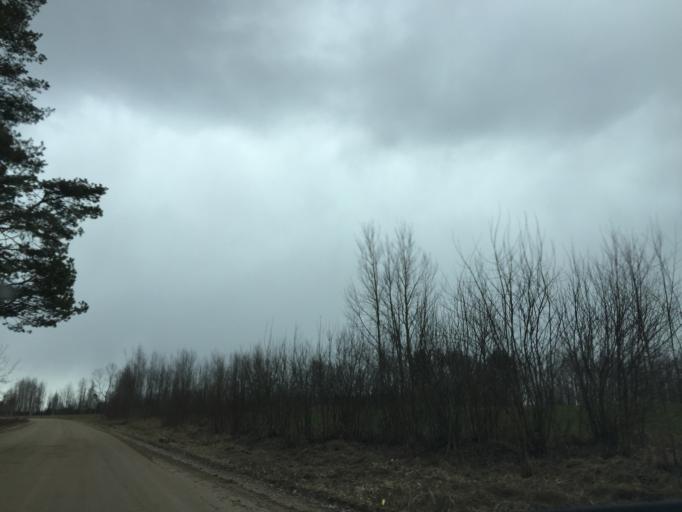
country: LV
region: Varkava
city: Vecvarkava
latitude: 56.0674
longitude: 26.5342
